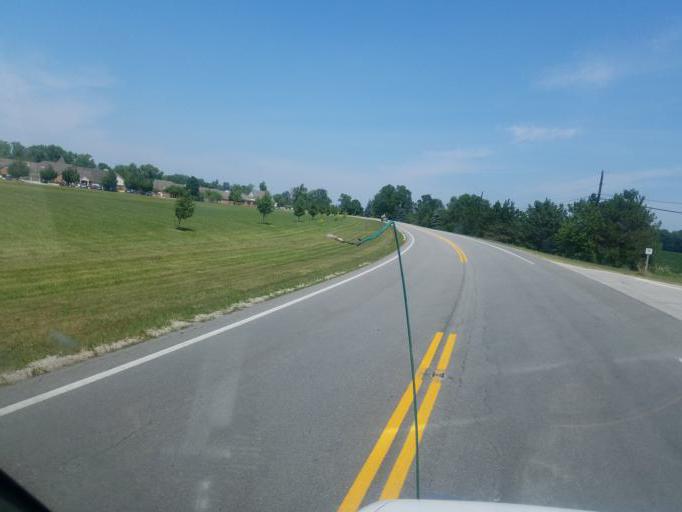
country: US
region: Ohio
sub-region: Auglaize County
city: Saint Marys
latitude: 40.5098
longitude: -84.4292
